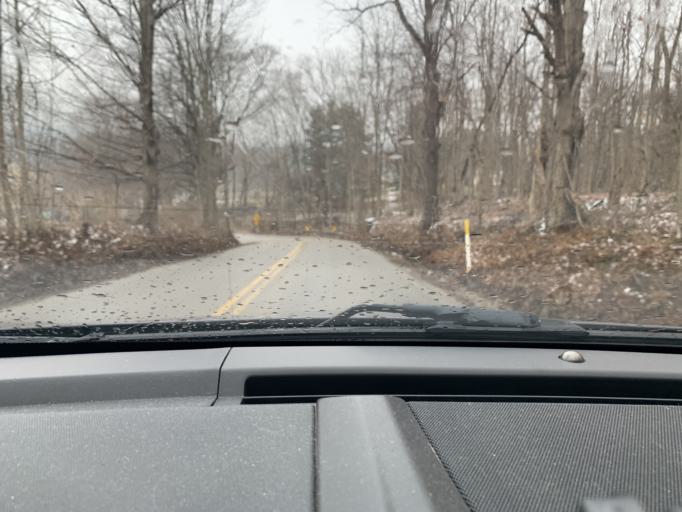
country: US
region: Ohio
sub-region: Ross County
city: Chillicothe
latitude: 39.3809
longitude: -82.9503
